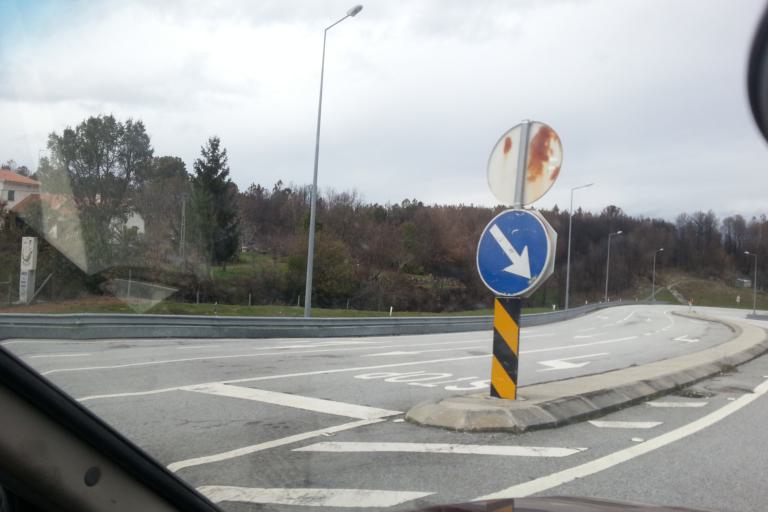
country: PT
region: Guarda
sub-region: Manteigas
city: Manteigas
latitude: 40.4761
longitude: -7.6002
